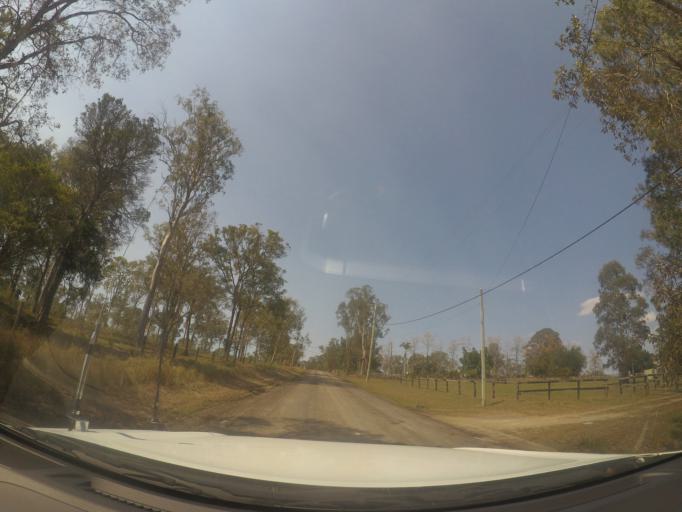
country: AU
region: Queensland
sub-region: Logan
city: Chambers Flat
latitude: -27.7602
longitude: 153.0593
